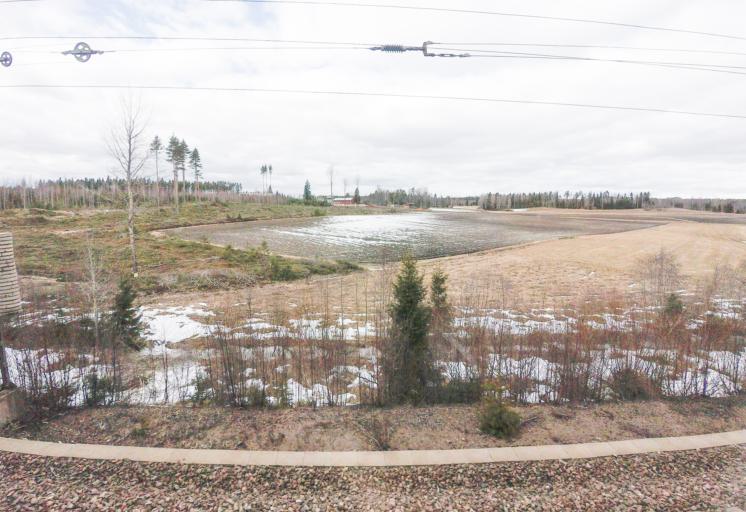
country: FI
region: South Karelia
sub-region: Lappeenranta
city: Luumaeki
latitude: 60.9119
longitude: 27.6133
